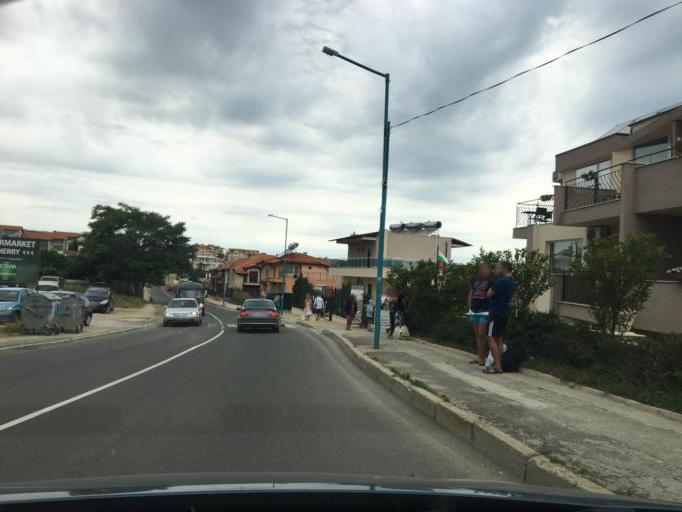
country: BG
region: Burgas
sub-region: Obshtina Sozopol
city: Sozopol
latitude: 42.4076
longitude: 27.7065
